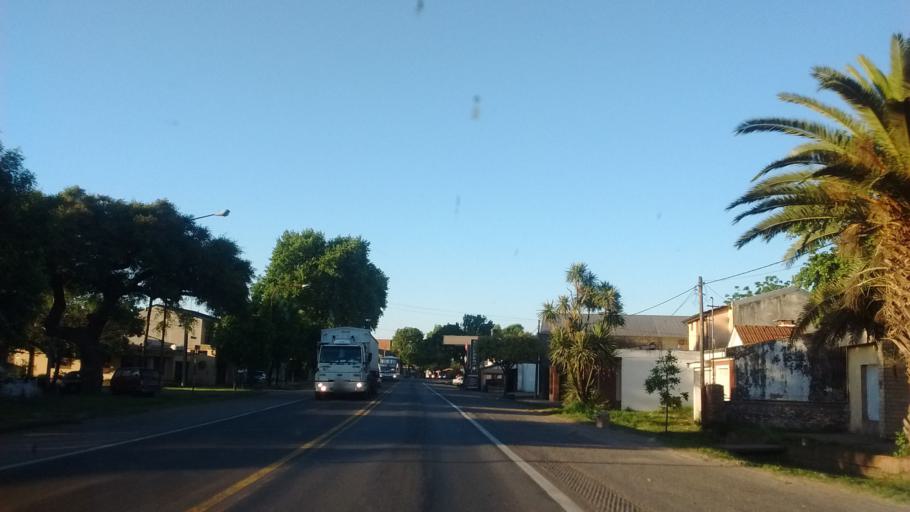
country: AR
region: Santa Fe
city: Firmat
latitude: -33.2380
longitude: -61.3539
